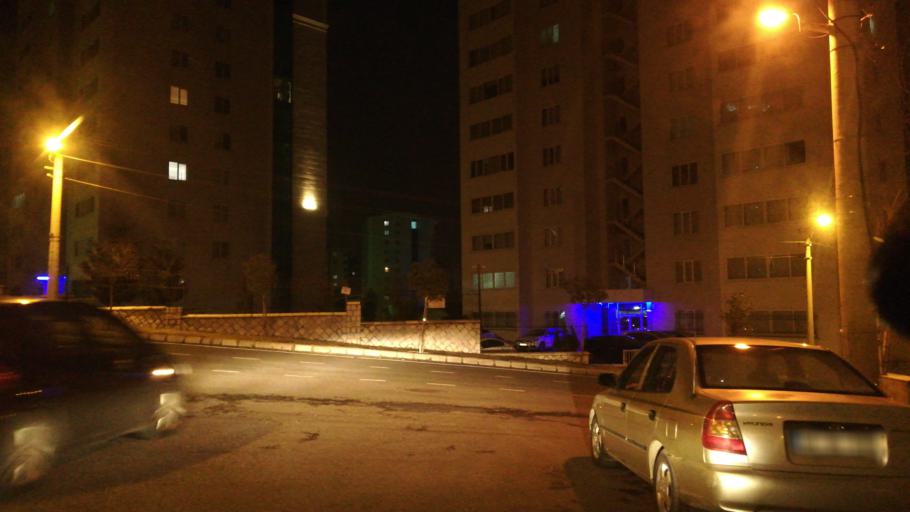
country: TR
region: Kahramanmaras
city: Kahramanmaras
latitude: 37.5971
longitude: 36.8875
